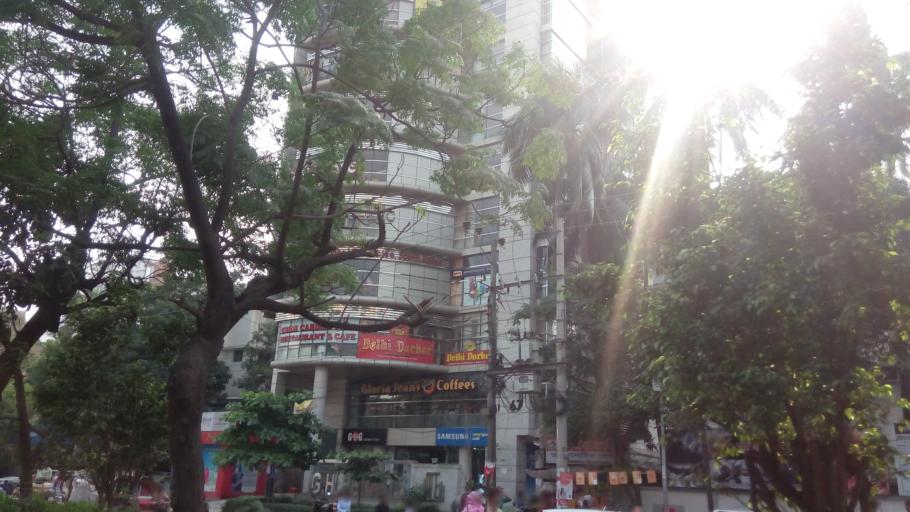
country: BD
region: Dhaka
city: Azimpur
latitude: 23.7501
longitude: 90.3688
